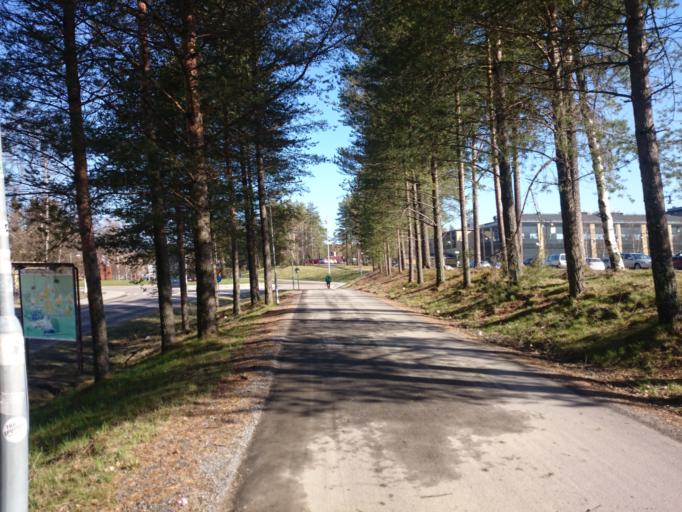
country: SE
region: Vaesterbotten
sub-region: Umea Kommun
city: Umea
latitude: 63.8172
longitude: 20.3045
